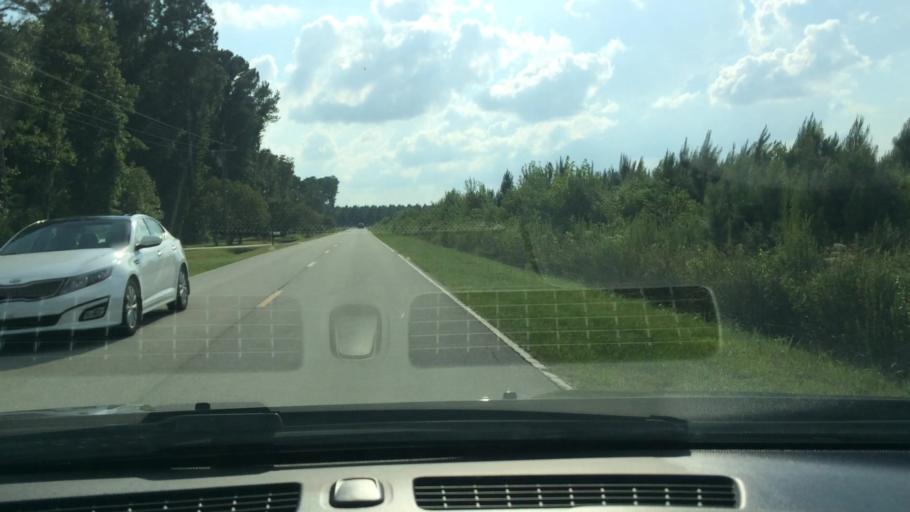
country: US
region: North Carolina
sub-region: Beaufort County
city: River Road
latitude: 35.4365
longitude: -77.0028
